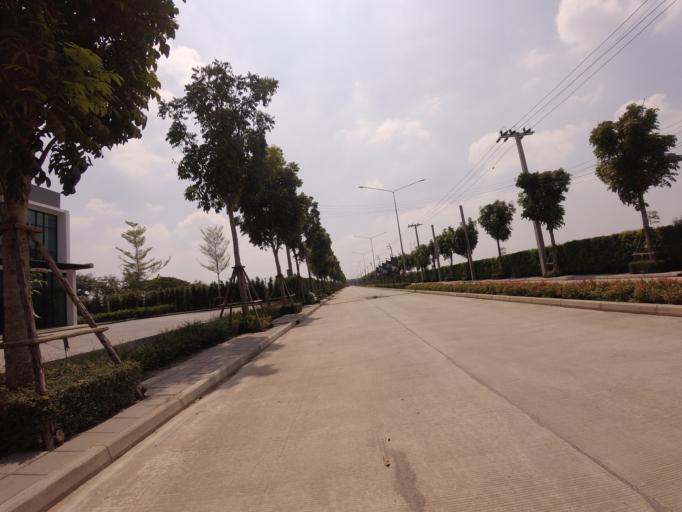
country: TH
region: Bangkok
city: Saphan Sung
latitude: 13.7534
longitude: 100.6707
